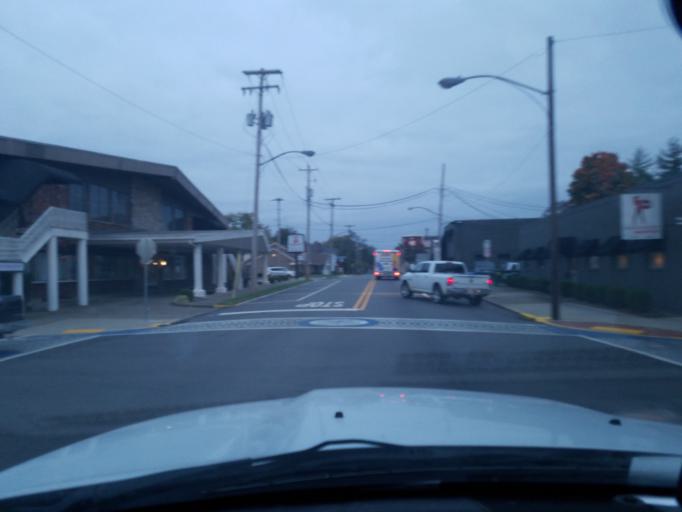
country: US
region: Indiana
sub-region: Floyd County
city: New Albany
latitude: 38.2874
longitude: -85.8227
